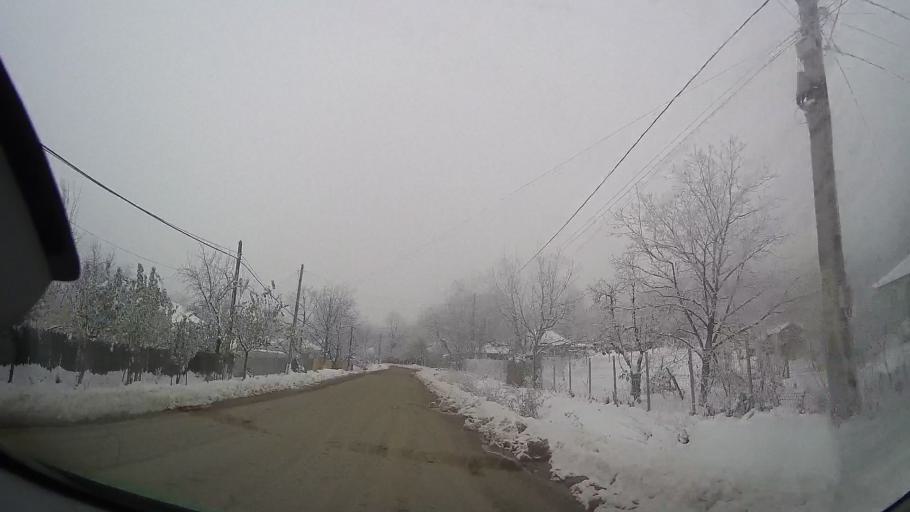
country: RO
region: Iasi
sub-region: Comuna Tansa
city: Tansa
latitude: 46.9049
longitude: 27.2425
